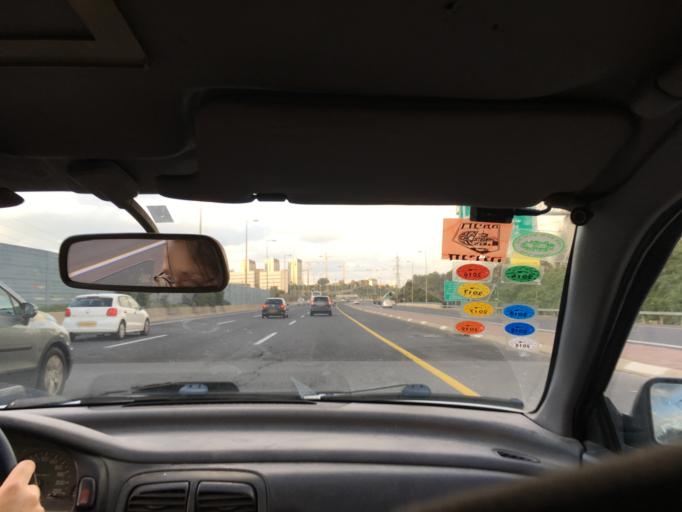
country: IL
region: Tel Aviv
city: Ramat Gan
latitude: 32.0975
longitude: 34.8026
